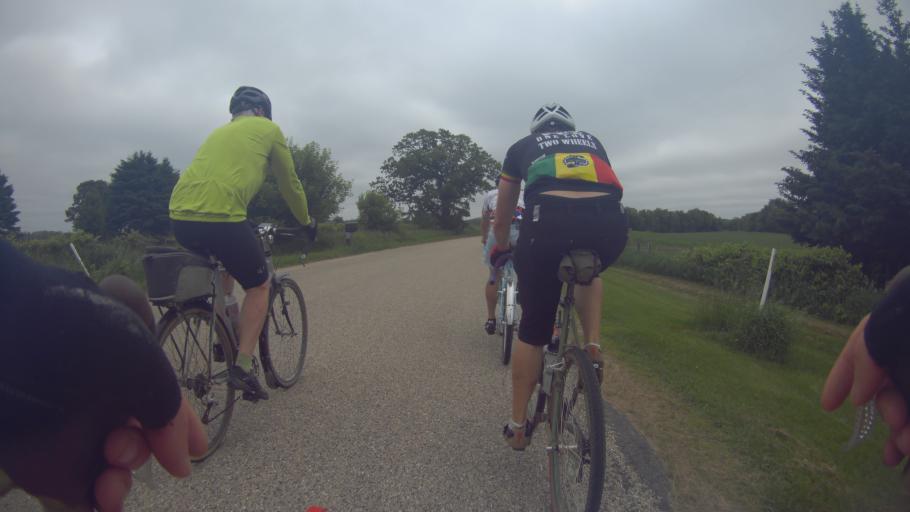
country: US
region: Wisconsin
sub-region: Dane County
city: Oregon
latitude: 42.8888
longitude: -89.3844
